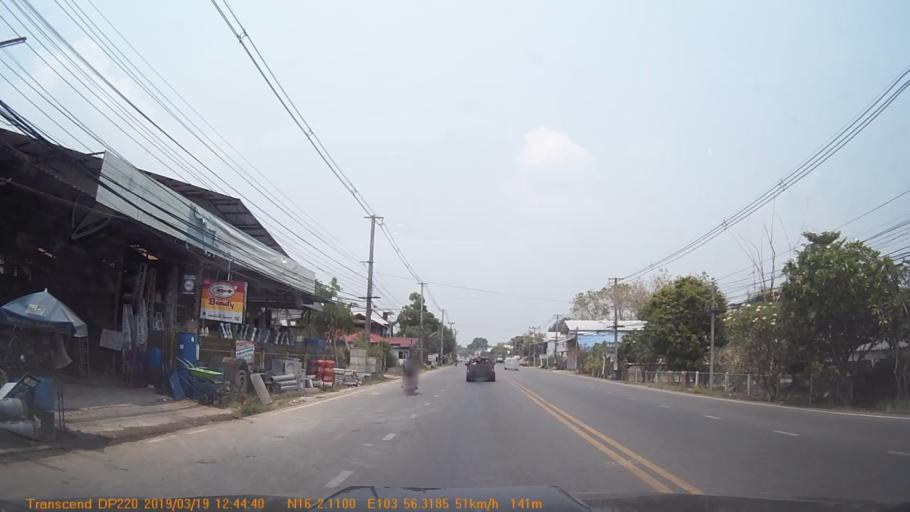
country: TH
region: Roi Et
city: Selaphum
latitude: 16.0354
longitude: 103.9386
